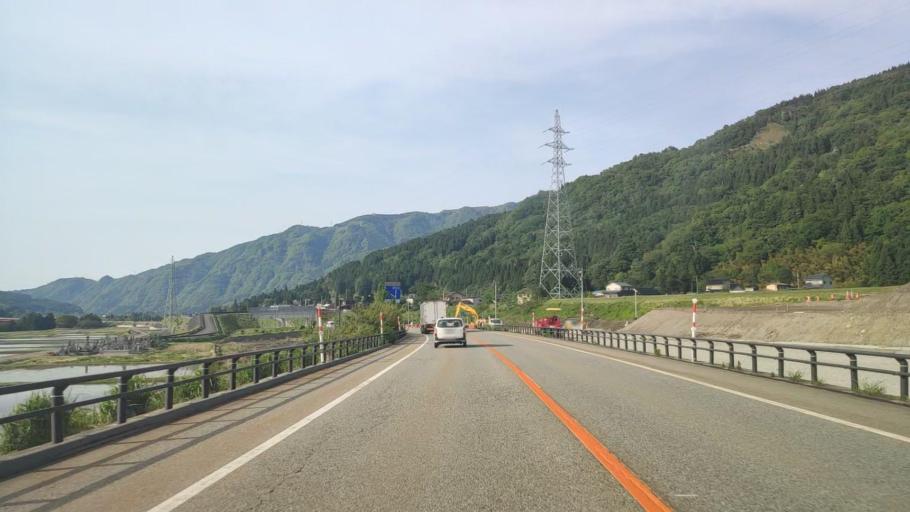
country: JP
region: Toyama
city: Yatsuomachi-higashikumisaka
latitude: 36.5167
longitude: 137.2302
